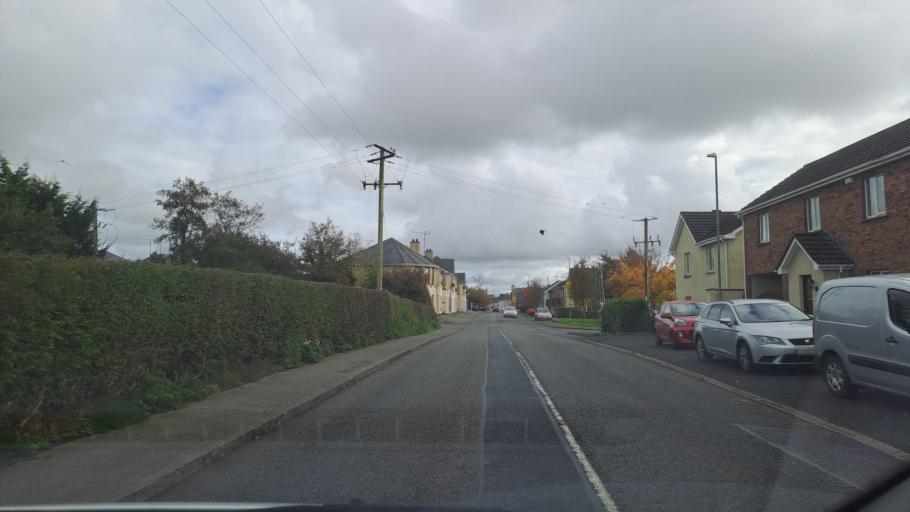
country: IE
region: Ulster
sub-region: An Cabhan
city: Mullagh
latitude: 53.8119
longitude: -6.9520
